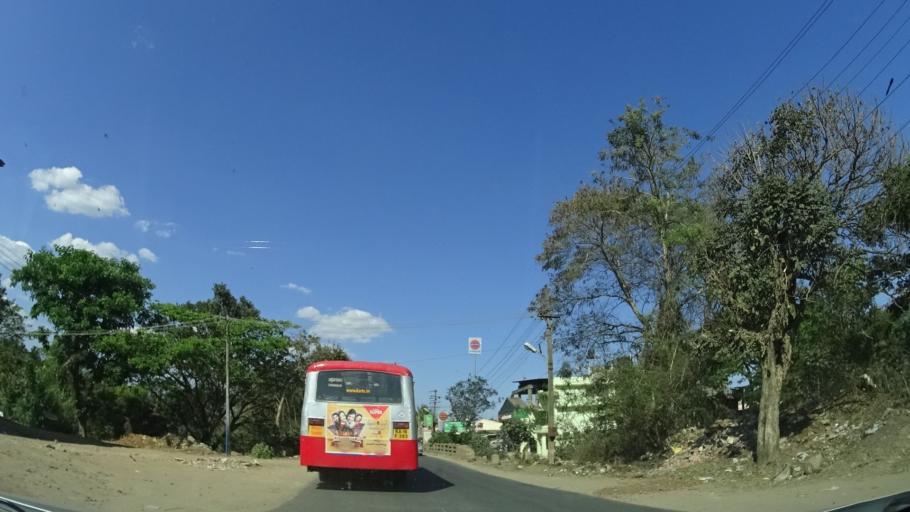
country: IN
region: Karnataka
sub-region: Chikmagalur
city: Chikmagalur
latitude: 13.3067
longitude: 75.7670
